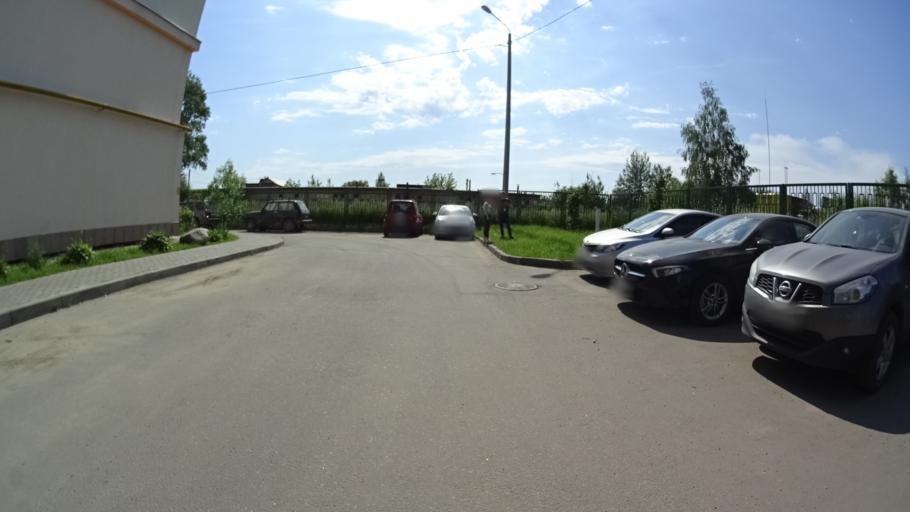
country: RU
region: Moskovskaya
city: Zelenogradskiy
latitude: 56.0846
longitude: 37.9336
